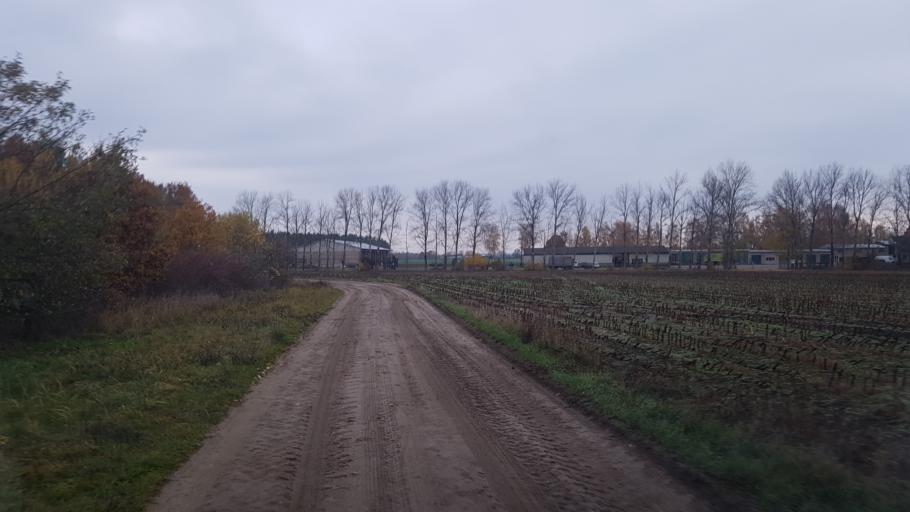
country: DE
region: Brandenburg
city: Doberlug-Kirchhain
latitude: 51.6568
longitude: 13.5162
